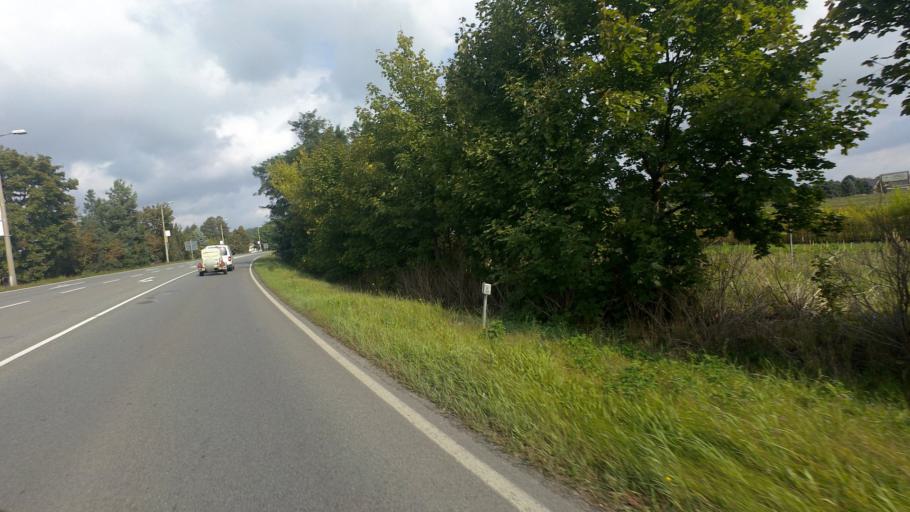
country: DE
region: Brandenburg
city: Elsterwerda
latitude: 51.4691
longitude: 13.4949
